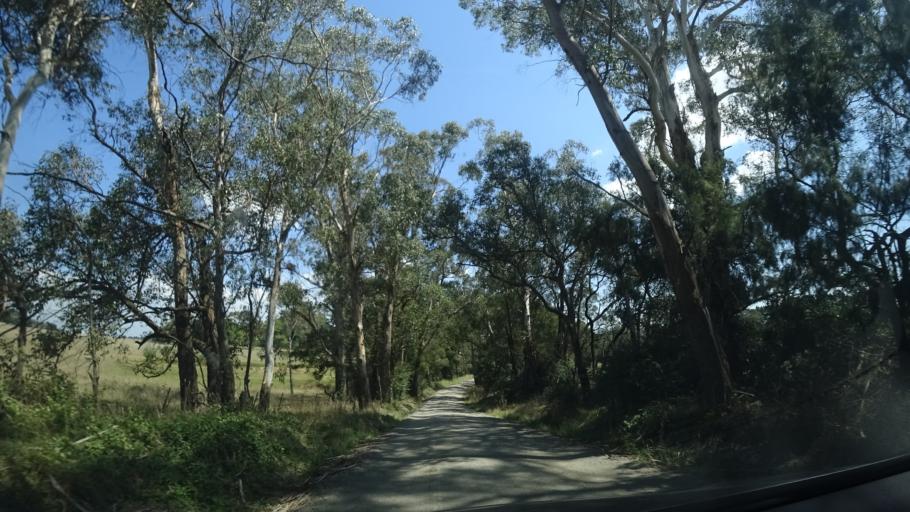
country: AU
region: New South Wales
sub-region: Wingecarribee
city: Bundanoon
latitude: -34.6227
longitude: 150.2689
